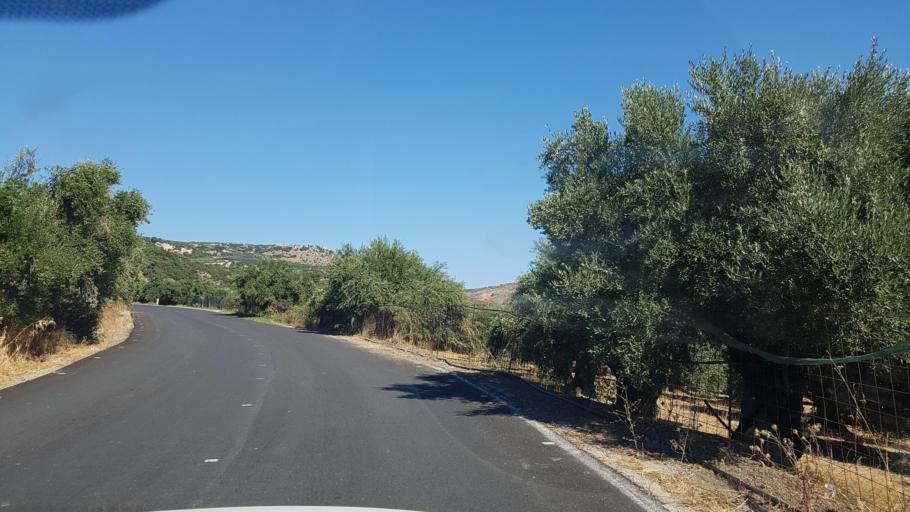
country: GR
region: Crete
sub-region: Nomos Chanias
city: Kissamos
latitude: 35.4951
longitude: 23.7198
